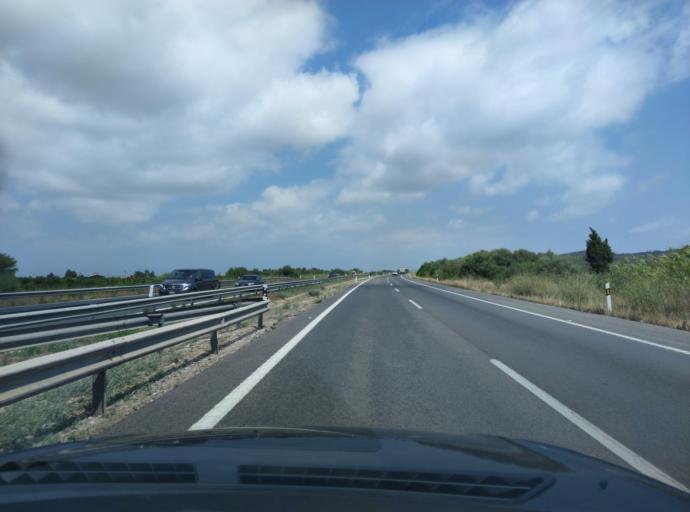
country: ES
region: Valencia
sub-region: Provincia de Castello
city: Vinaros
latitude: 40.4910
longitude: 0.4151
